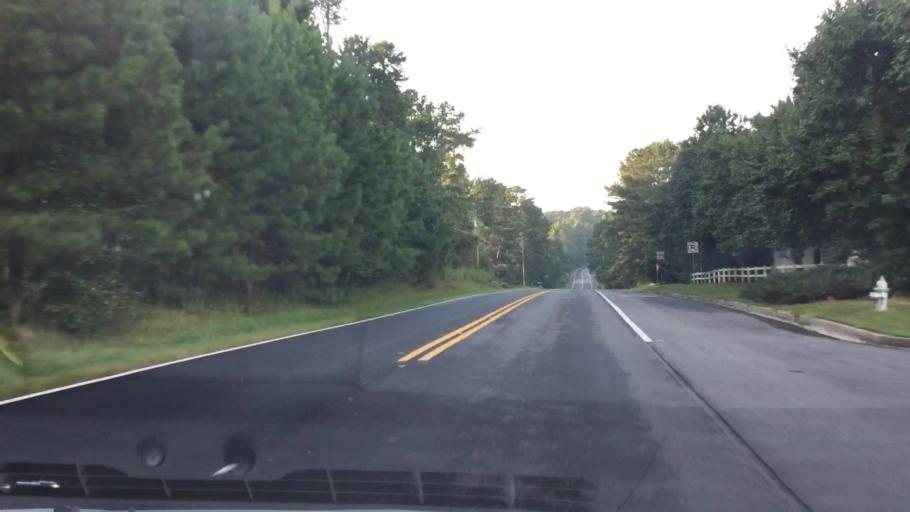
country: US
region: Georgia
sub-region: Henry County
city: McDonough
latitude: 33.4649
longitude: -84.1932
